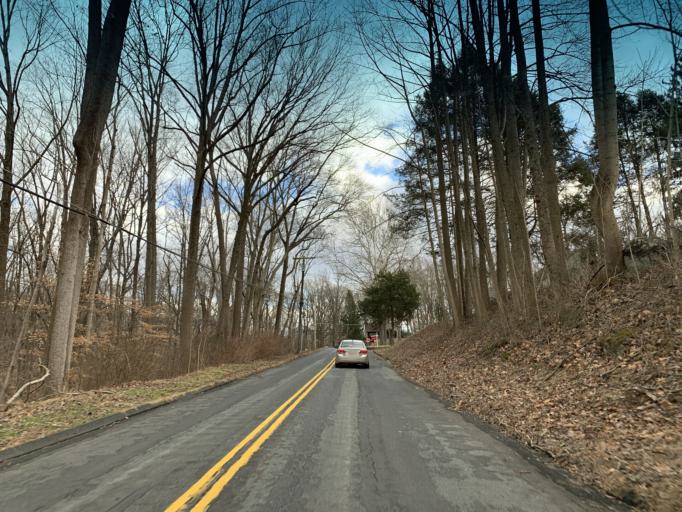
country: US
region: Maryland
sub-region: Harford County
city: South Bel Air
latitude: 39.6097
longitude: -76.3097
